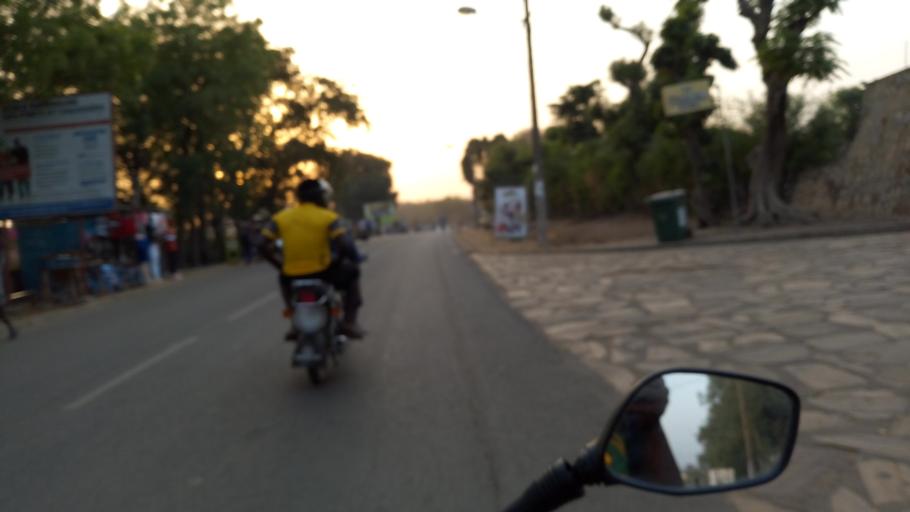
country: TG
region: Kara
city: Kara
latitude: 9.5493
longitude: 1.1831
